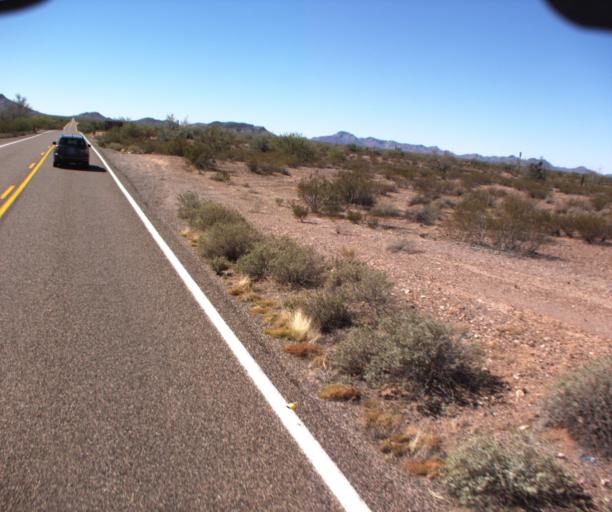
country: US
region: Arizona
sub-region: Pima County
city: Ajo
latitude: 32.1393
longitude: -112.7666
